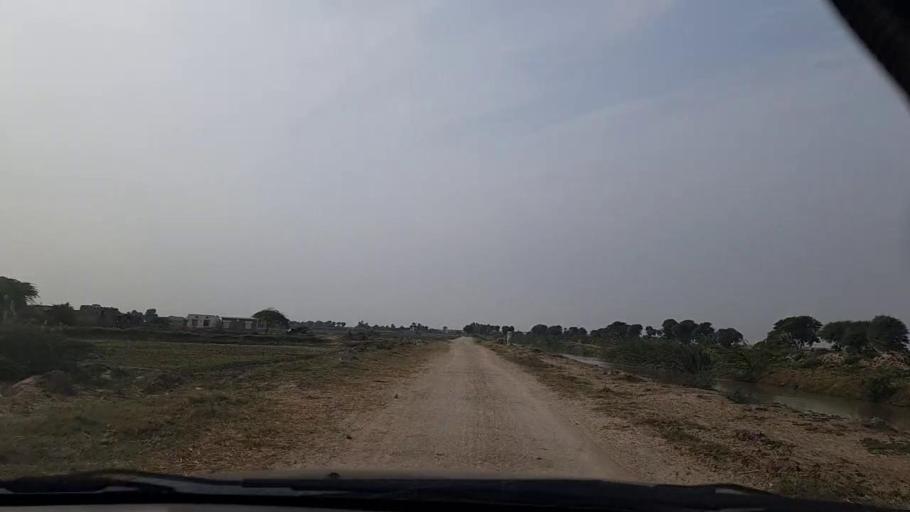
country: PK
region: Sindh
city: Thatta
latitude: 24.5781
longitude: 67.8892
